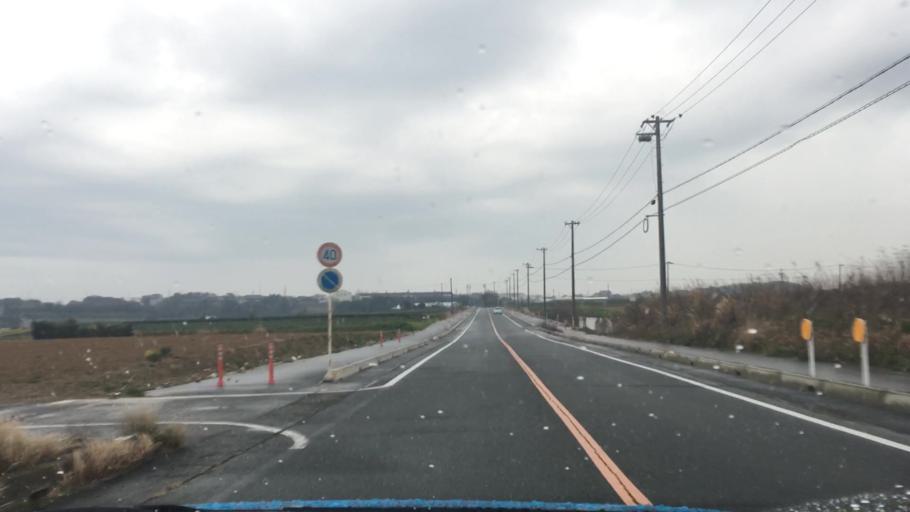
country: JP
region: Aichi
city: Toyohashi
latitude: 34.6735
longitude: 137.3908
